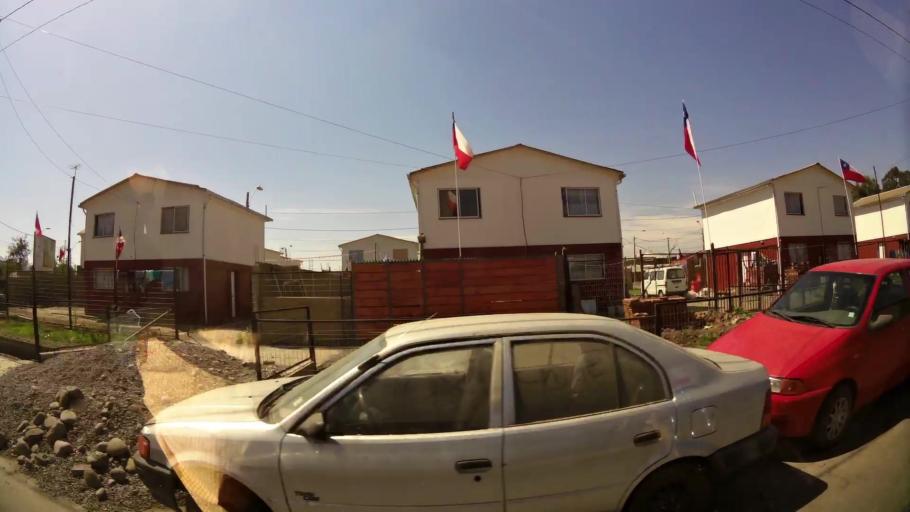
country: CL
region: Santiago Metropolitan
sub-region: Provincia de Talagante
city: Talagante
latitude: -33.6549
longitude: -70.9282
